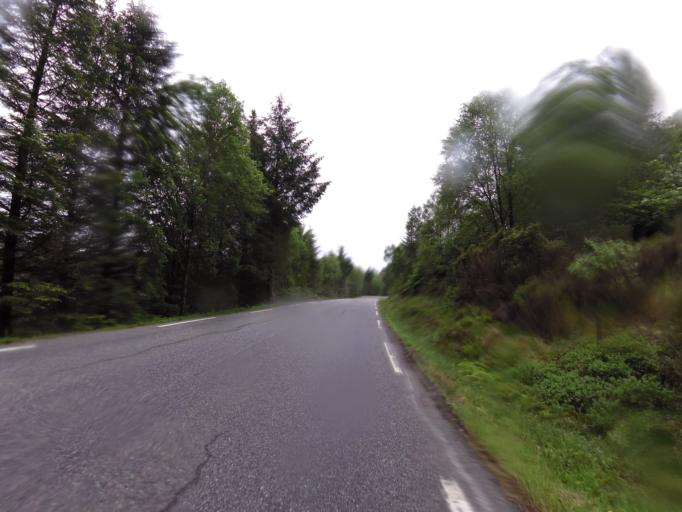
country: NO
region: Hordaland
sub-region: Sveio
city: Sveio
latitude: 59.5198
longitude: 5.2849
